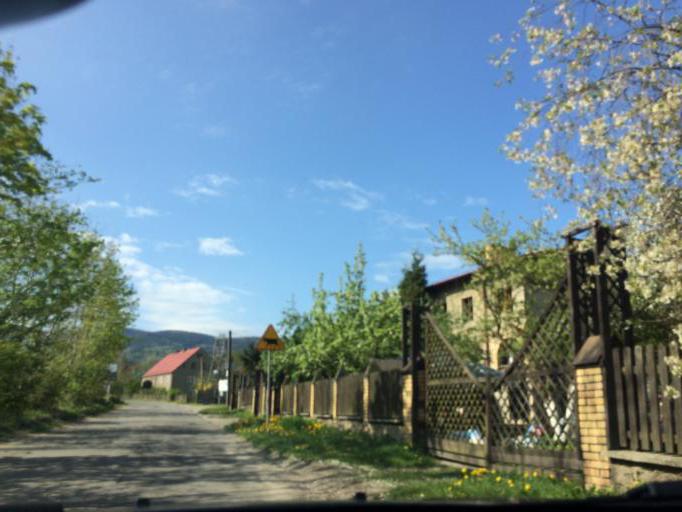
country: PL
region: Lower Silesian Voivodeship
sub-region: Powiat dzierzoniowski
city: Pieszyce
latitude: 50.6837
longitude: 16.5438
